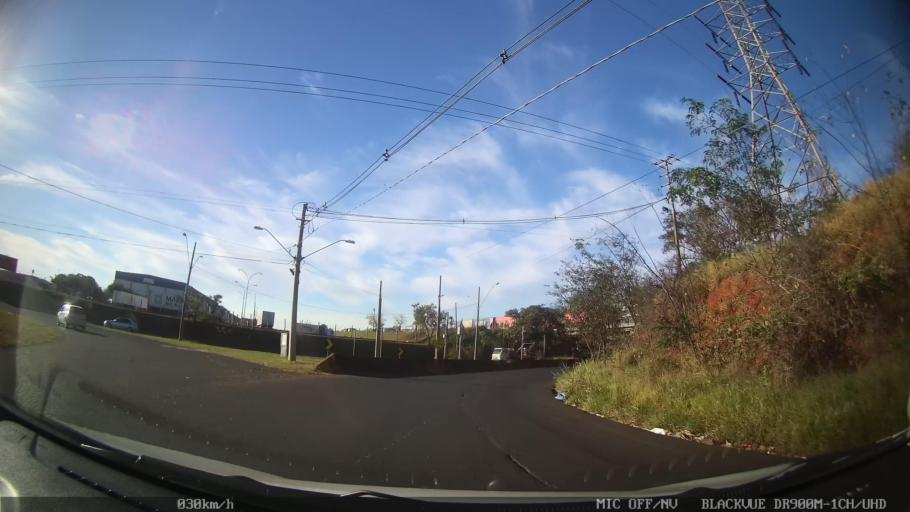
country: BR
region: Sao Paulo
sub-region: Americo Brasiliense
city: Americo Brasiliense
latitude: -21.7476
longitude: -48.1341
